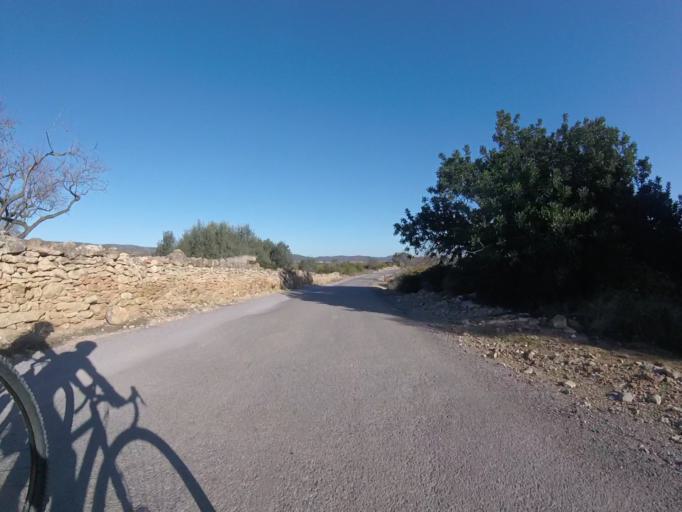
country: ES
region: Valencia
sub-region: Provincia de Castello
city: Alcala de Xivert
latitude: 40.2921
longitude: 0.2170
